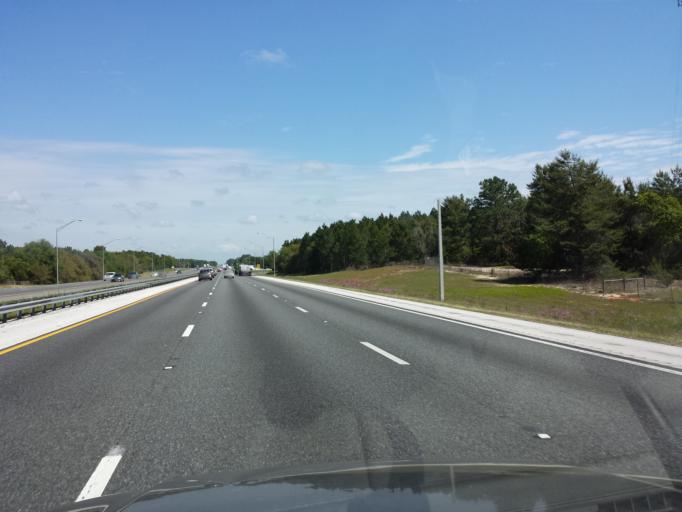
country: US
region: Florida
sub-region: Marion County
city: Ocala
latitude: 29.0864
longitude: -82.1849
